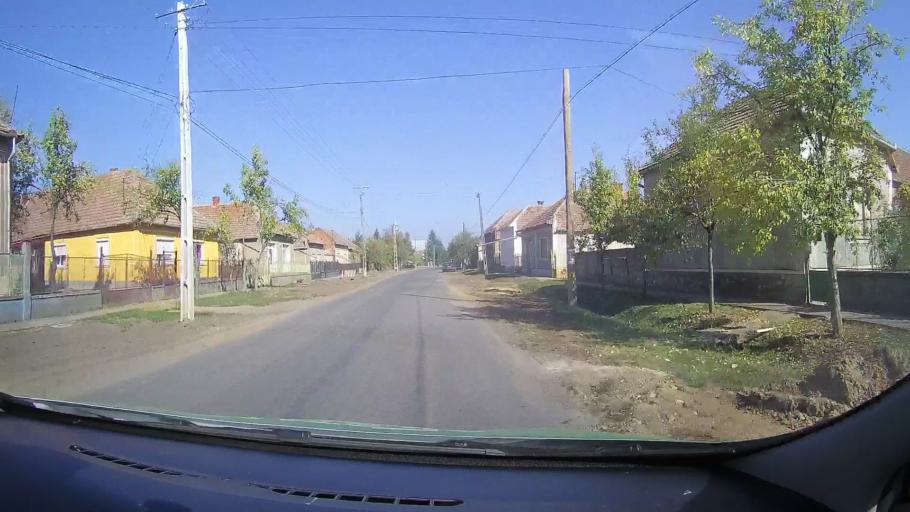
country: RO
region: Satu Mare
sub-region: Comuna Ciumesti
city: Ciumesti
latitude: 47.6651
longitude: 22.3369
